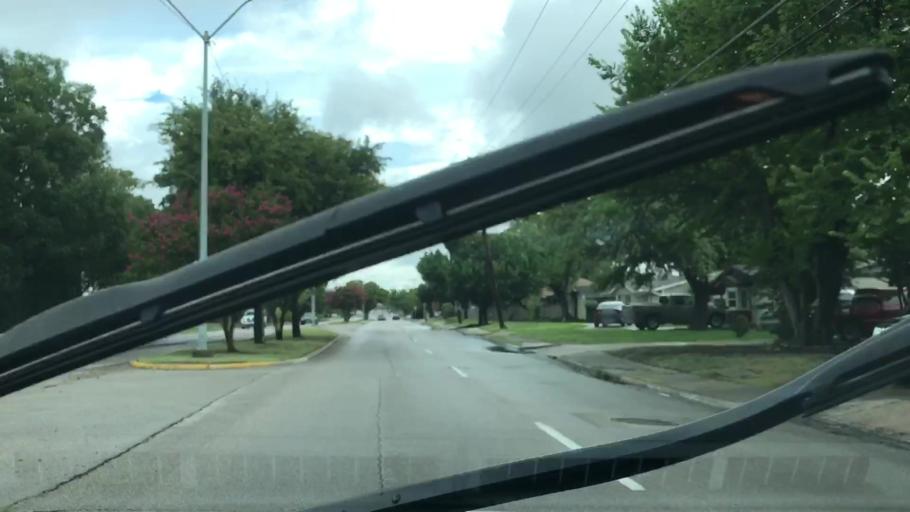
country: US
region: Texas
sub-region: Dallas County
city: Irving
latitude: 32.8456
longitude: -96.9765
